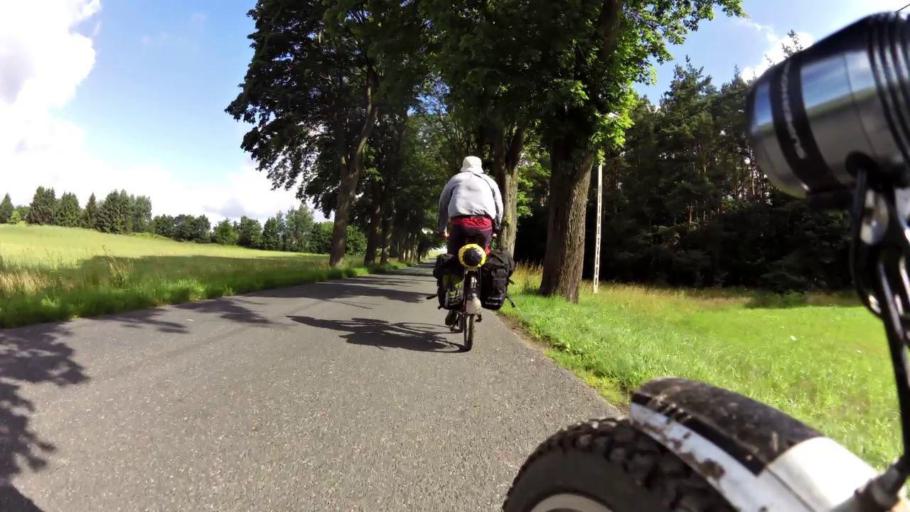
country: PL
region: West Pomeranian Voivodeship
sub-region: Powiat swidwinski
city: Rabino
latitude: 53.7610
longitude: 15.9110
